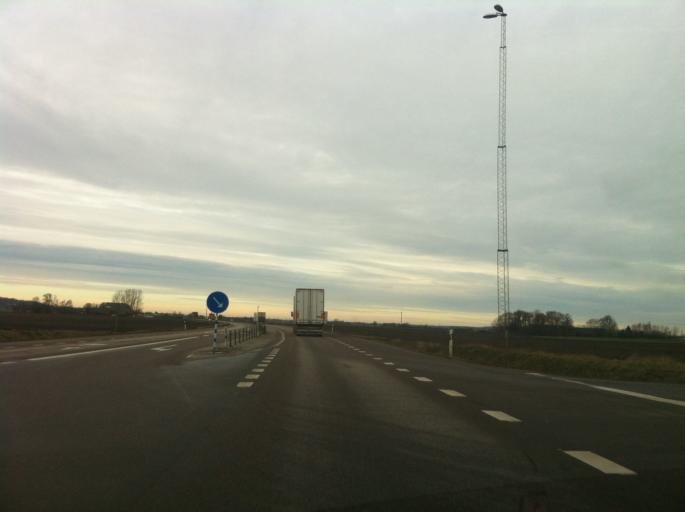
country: SE
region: Skane
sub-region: Astorps Kommun
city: Kvidinge
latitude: 56.1330
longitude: 13.0320
